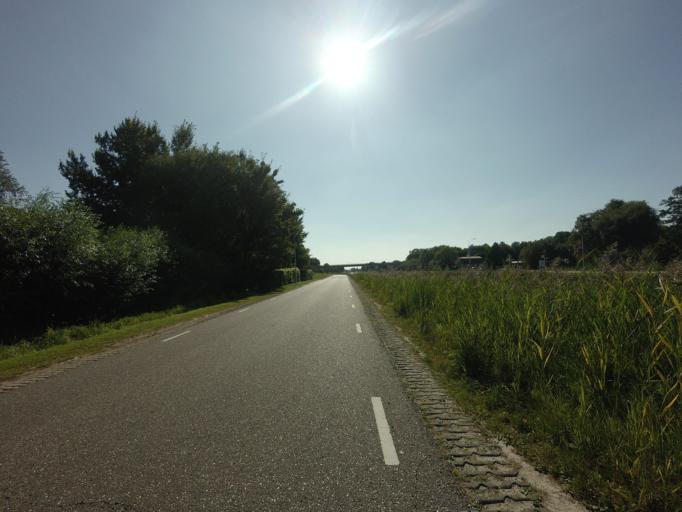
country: NL
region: Overijssel
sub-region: Gemeente Hardenberg
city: Hardenberg
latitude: 52.5332
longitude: 6.6278
